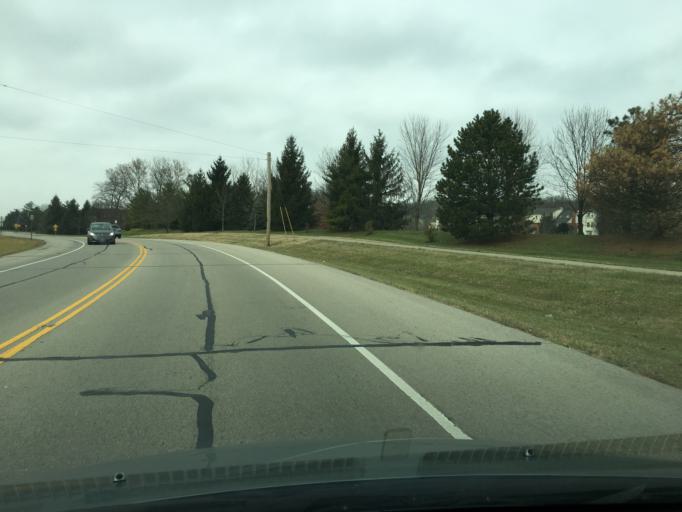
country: US
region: Ohio
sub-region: Butler County
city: Beckett Ridge
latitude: 39.3297
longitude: -84.4252
